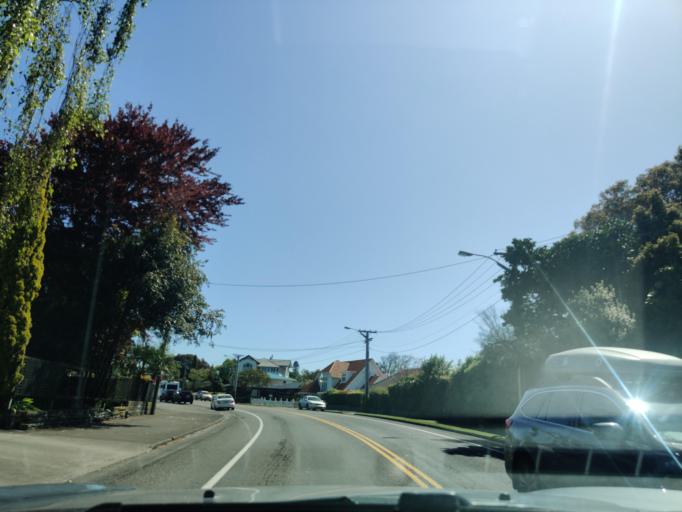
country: NZ
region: Manawatu-Wanganui
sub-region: Wanganui District
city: Wanganui
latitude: -39.9196
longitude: 175.0390
